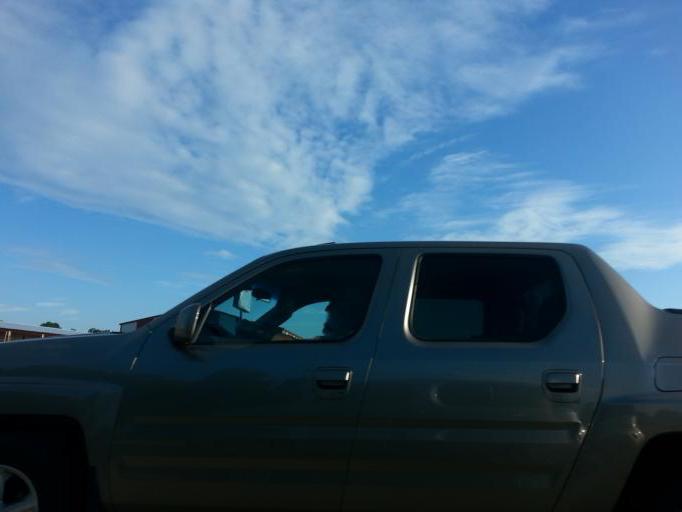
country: US
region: Alabama
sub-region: Lauderdale County
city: Killen
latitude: 34.8597
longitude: -87.4369
